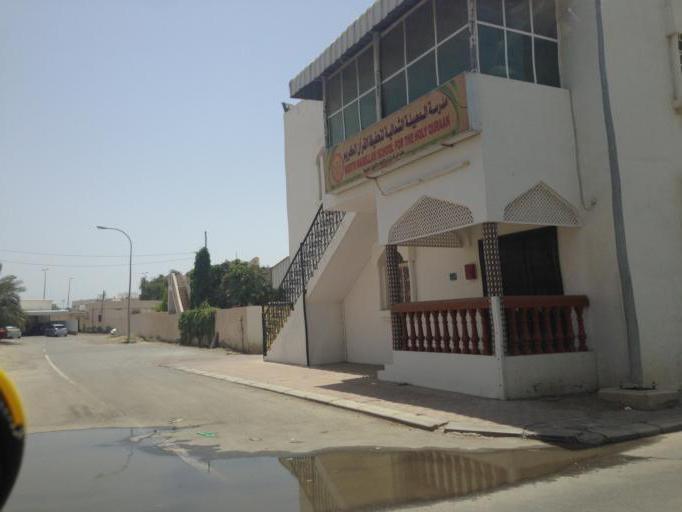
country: OM
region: Muhafazat Masqat
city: As Sib al Jadidah
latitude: 23.6796
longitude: 58.1266
